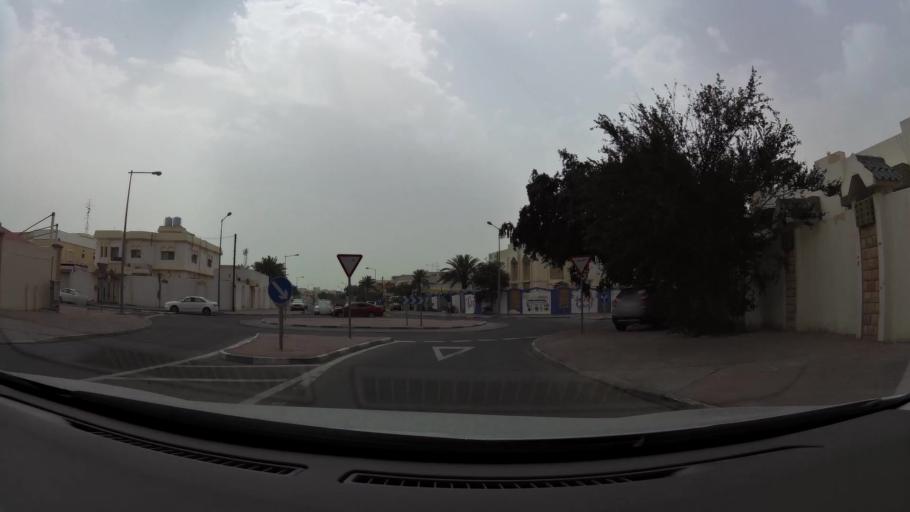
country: QA
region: Baladiyat ad Dawhah
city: Doha
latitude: 25.2599
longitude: 51.5428
